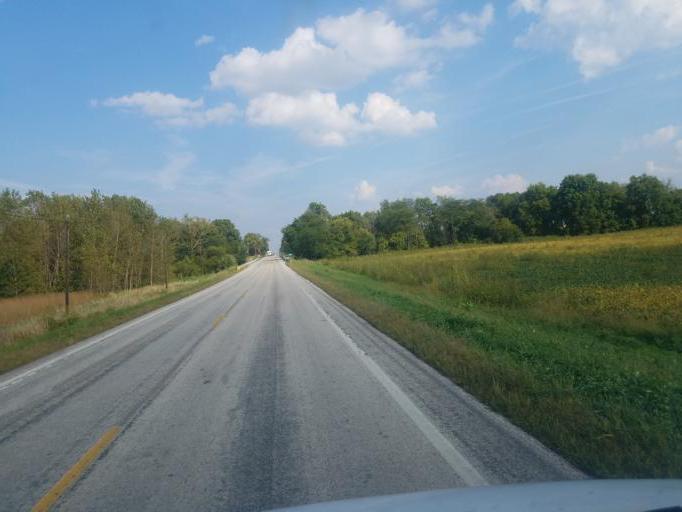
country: US
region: Ohio
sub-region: Hancock County
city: Arlington
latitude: 40.8912
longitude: -83.5663
